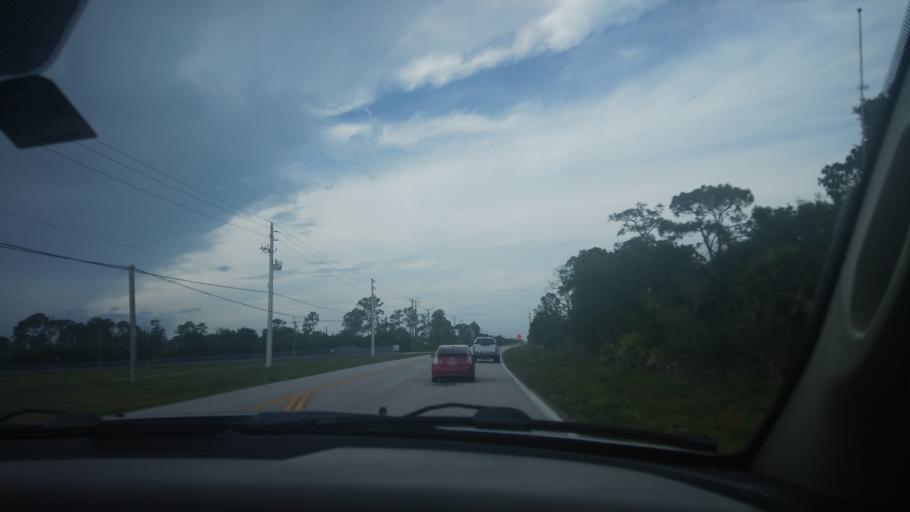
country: US
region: Florida
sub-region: Brevard County
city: Grant-Valkaria
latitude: 27.9086
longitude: -80.6232
